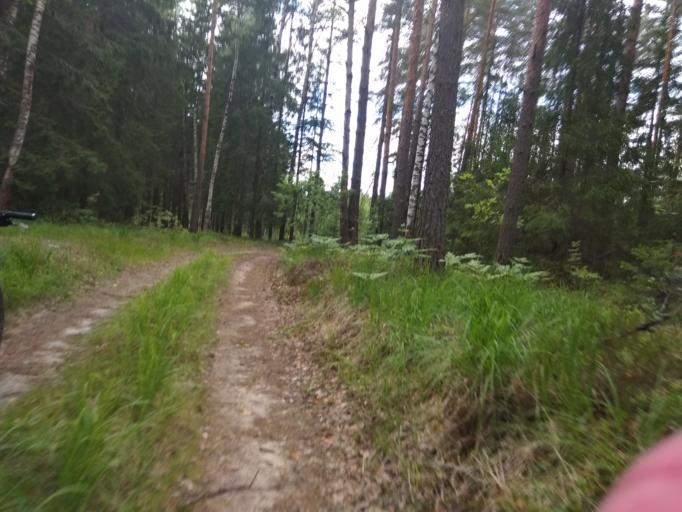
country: RU
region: Moskovskaya
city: Misheronskiy
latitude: 55.6376
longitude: 39.7215
